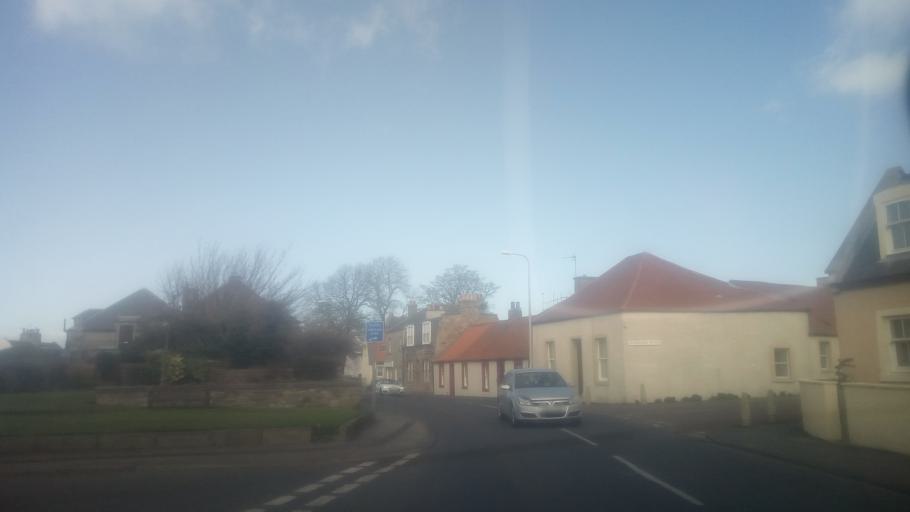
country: GB
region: Scotland
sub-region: East Lothian
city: Tranent
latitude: 55.9458
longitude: -2.9544
